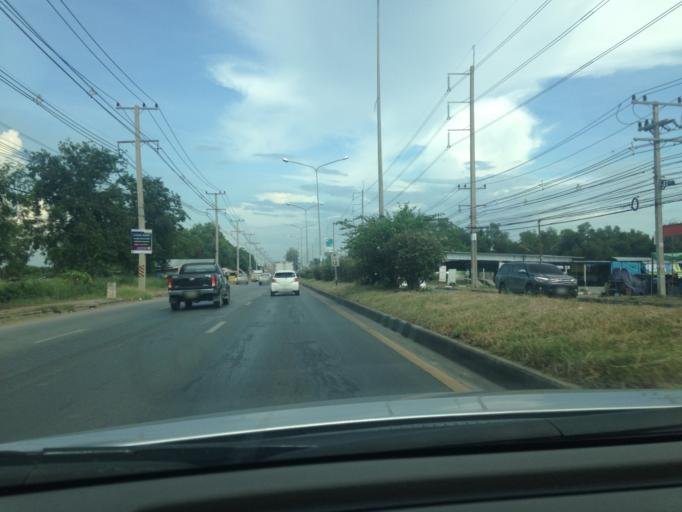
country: TH
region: Pathum Thani
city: Khlong Luang
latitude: 14.0666
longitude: 100.6816
